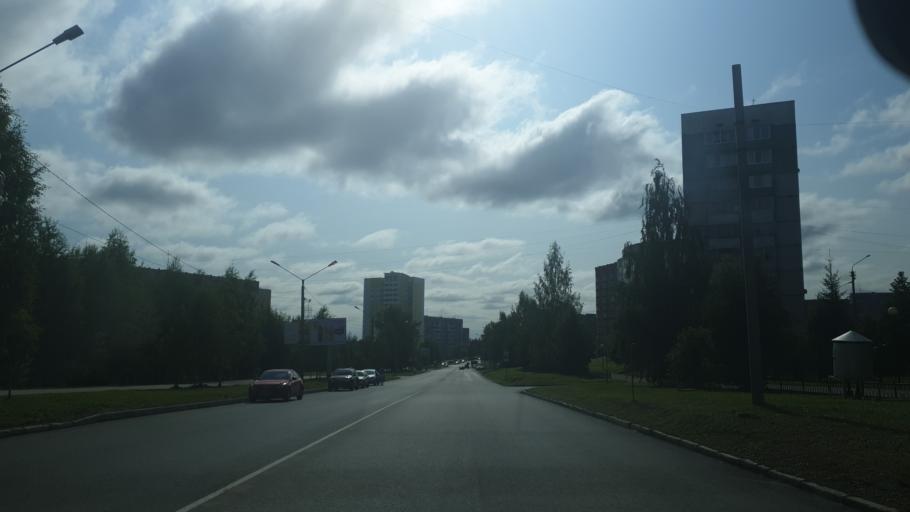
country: RU
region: Komi Republic
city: Ezhva
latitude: 61.7878
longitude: 50.7529
